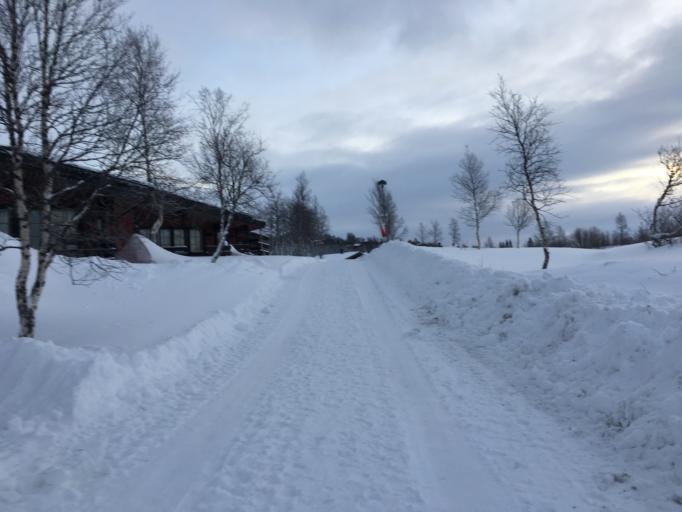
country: NO
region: Nord-Trondelag
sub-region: Meraker
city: Meraker
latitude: 63.3198
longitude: 12.0874
